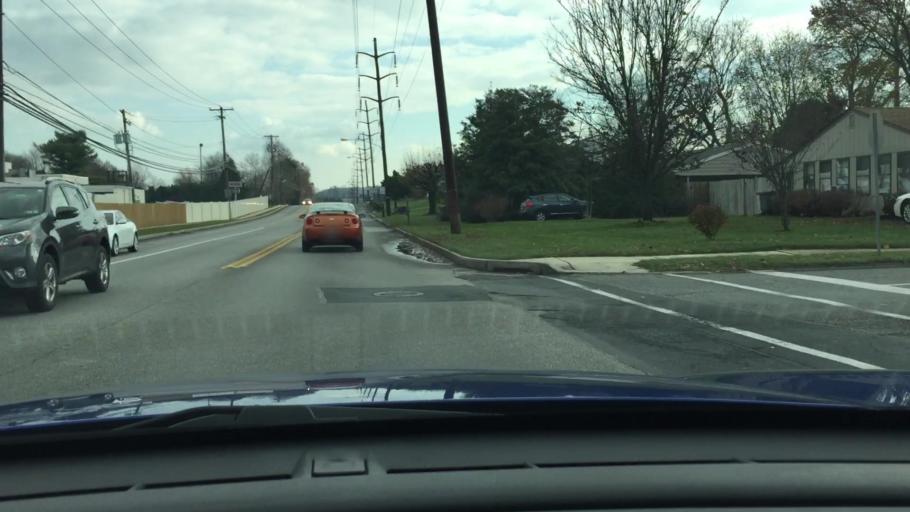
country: US
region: Pennsylvania
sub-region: Cumberland County
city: Shiremanstown
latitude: 40.2178
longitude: -76.9770
